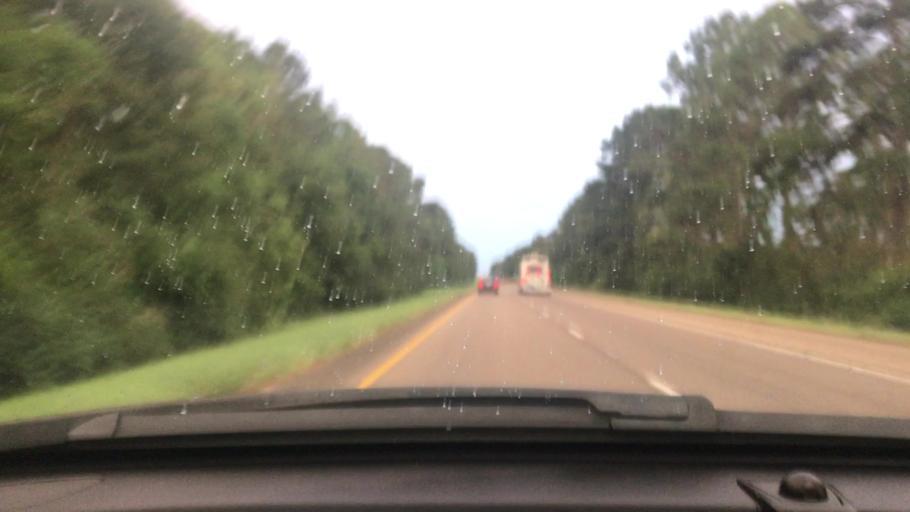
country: US
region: Louisiana
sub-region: Tangipahoa Parish
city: Roseland
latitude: 30.7969
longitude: -90.5333
